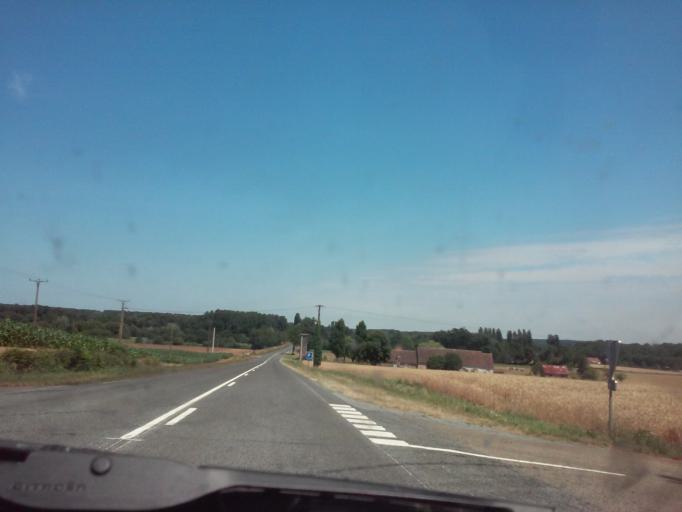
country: FR
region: Pays de la Loire
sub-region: Departement de la Sarthe
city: Beaufay
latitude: 48.1210
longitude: 0.3603
